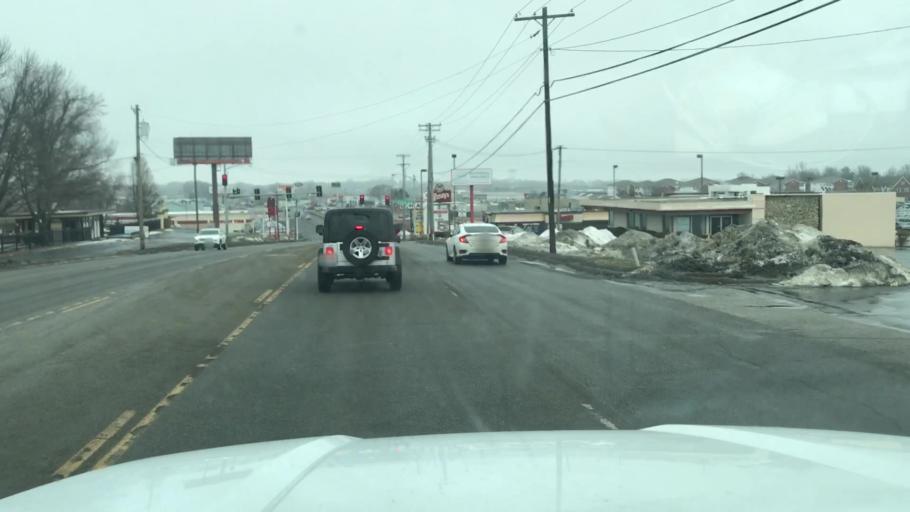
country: US
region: Missouri
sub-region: Buchanan County
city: Saint Joseph
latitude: 39.7800
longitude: -94.8030
